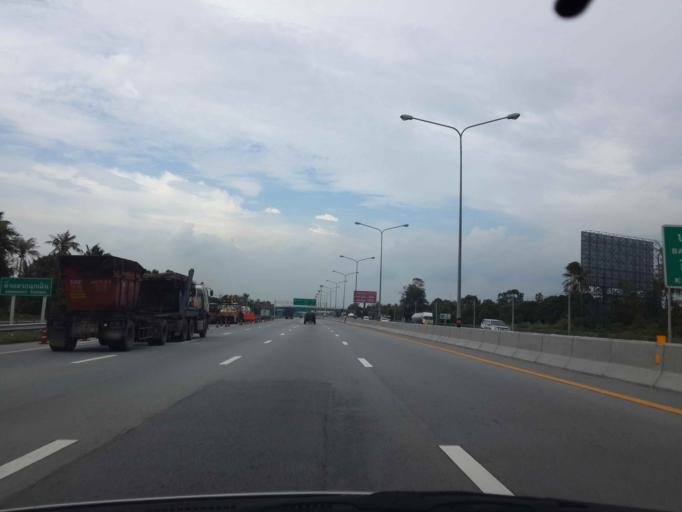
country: TH
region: Chon Buri
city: Chon Buri
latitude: 13.3277
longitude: 101.0173
